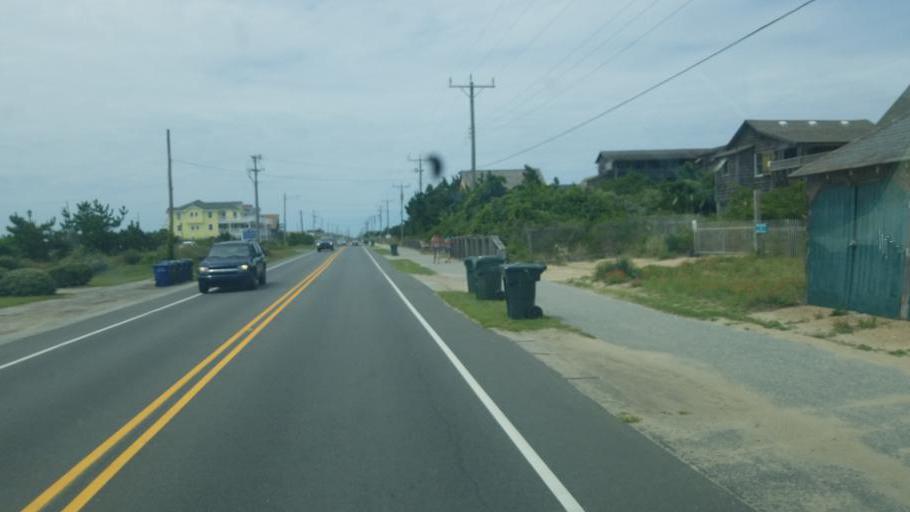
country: US
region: North Carolina
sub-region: Dare County
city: Nags Head
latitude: 35.9498
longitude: -75.6199
